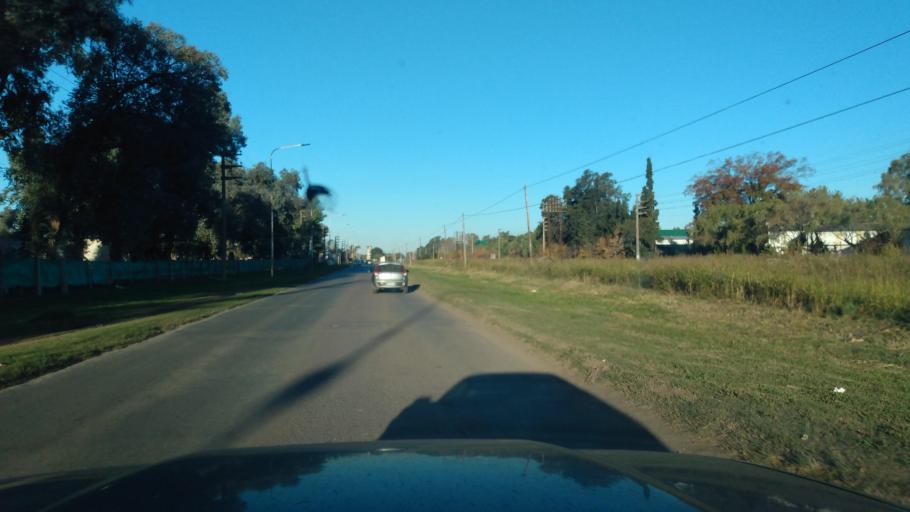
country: AR
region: Buenos Aires
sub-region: Partido de General Rodriguez
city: General Rodriguez
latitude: -34.6268
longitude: -58.8749
